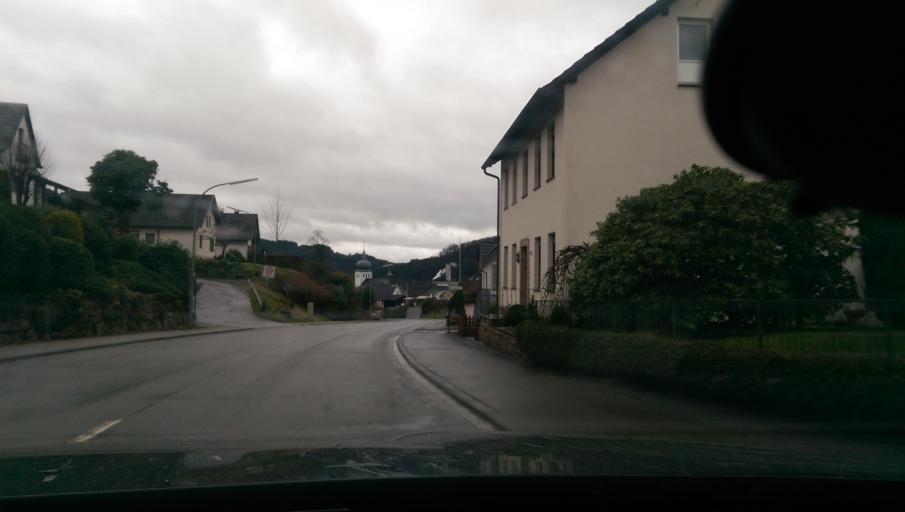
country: DE
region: North Rhine-Westphalia
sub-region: Regierungsbezirk Arnsberg
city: Finnentrop
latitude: 51.2201
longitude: 7.9542
